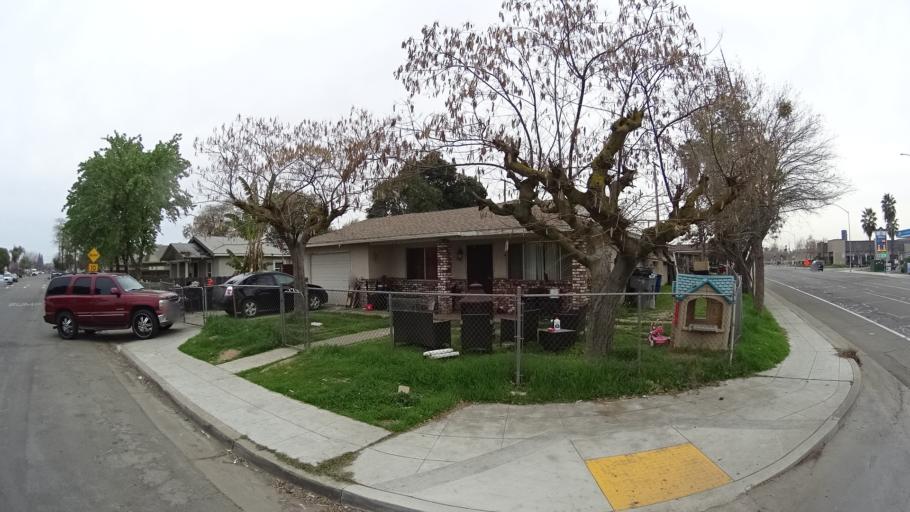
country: US
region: California
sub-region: Fresno County
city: Fresno
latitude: 36.8417
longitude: -119.8018
